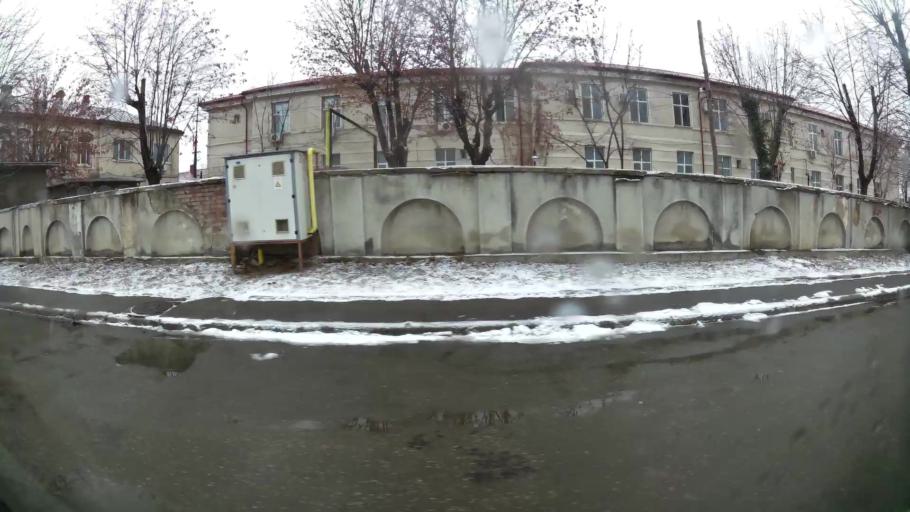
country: RO
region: Prahova
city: Ploiesti
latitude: 44.9499
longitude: 26.0240
